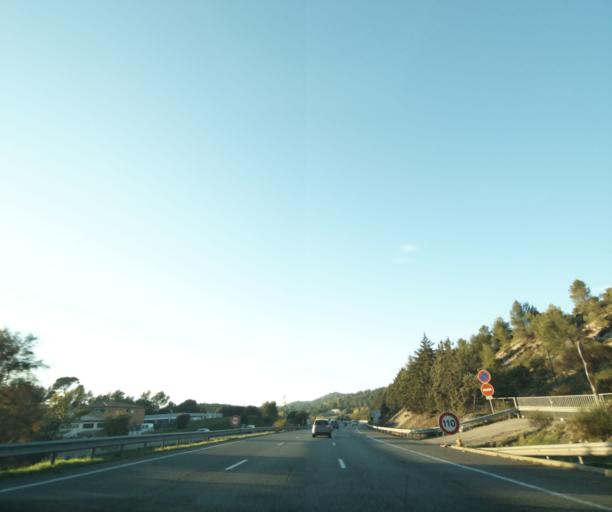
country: FR
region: Provence-Alpes-Cote d'Azur
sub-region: Departement des Bouches-du-Rhone
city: Le Tholonet
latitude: 43.5088
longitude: 5.4997
